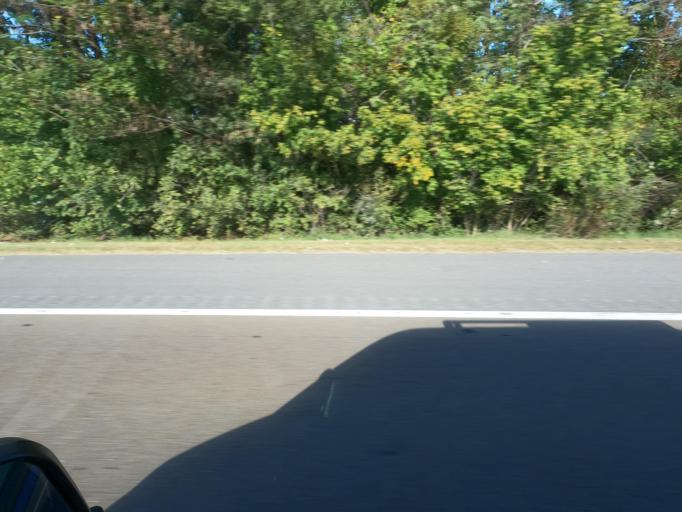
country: US
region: Tennessee
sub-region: Tipton County
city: Munford
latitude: 35.4070
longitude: -89.8379
